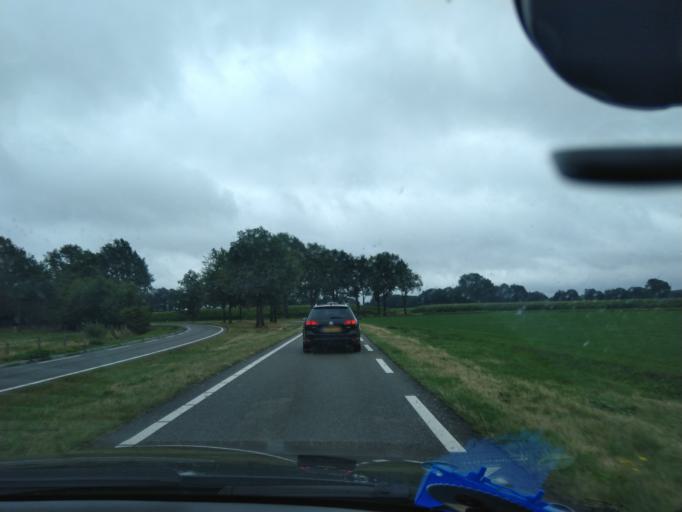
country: DE
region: Lower Saxony
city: Nordhorn
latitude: 52.3684
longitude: 7.0084
